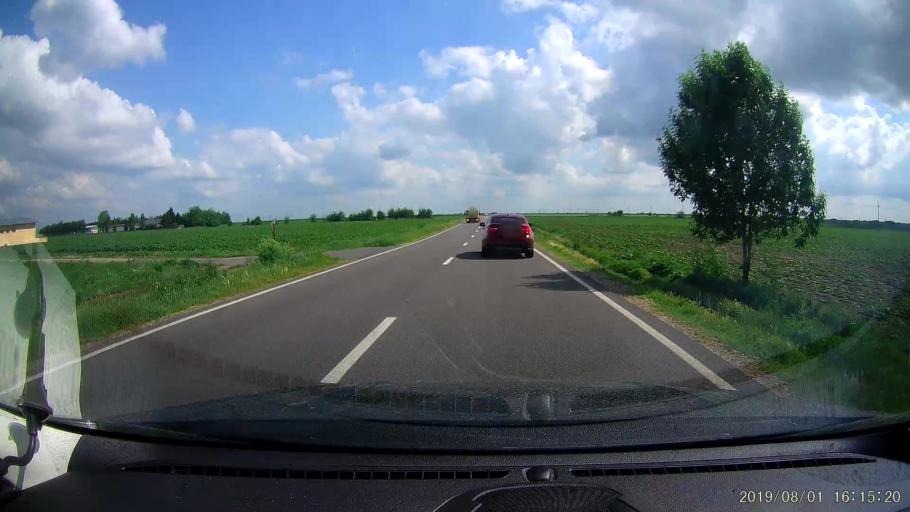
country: RO
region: Calarasi
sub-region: Comuna Stefan Voda
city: Stefan Voda
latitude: 44.3395
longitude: 27.3614
